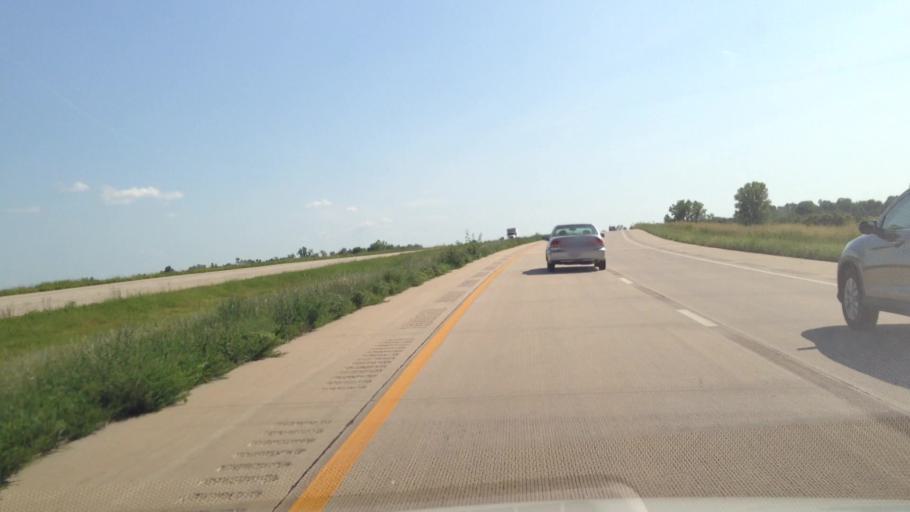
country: US
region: Kansas
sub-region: Bourbon County
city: Fort Scott
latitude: 37.9703
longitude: -94.7050
